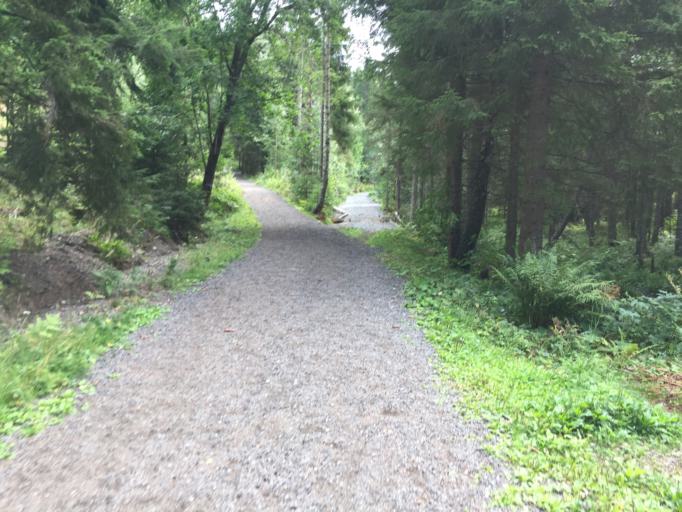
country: NO
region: Akershus
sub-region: Raelingen
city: Fjerdingby
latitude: 59.9154
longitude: 11.0165
